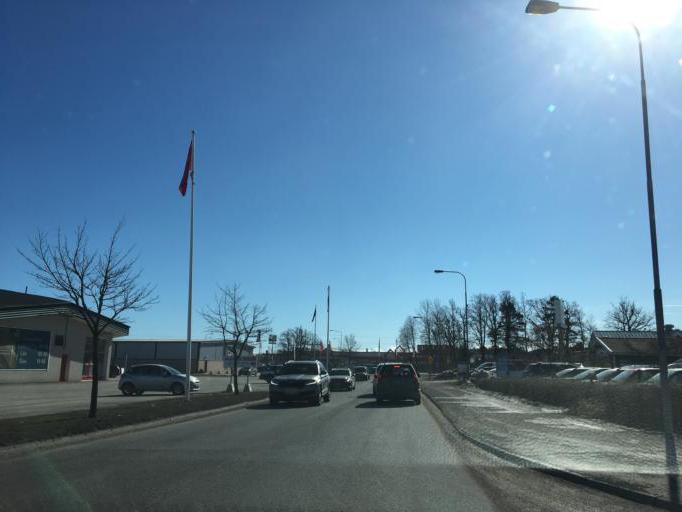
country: SE
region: Vaestmanland
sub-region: Vasteras
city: Vasteras
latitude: 59.6140
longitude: 16.4665
